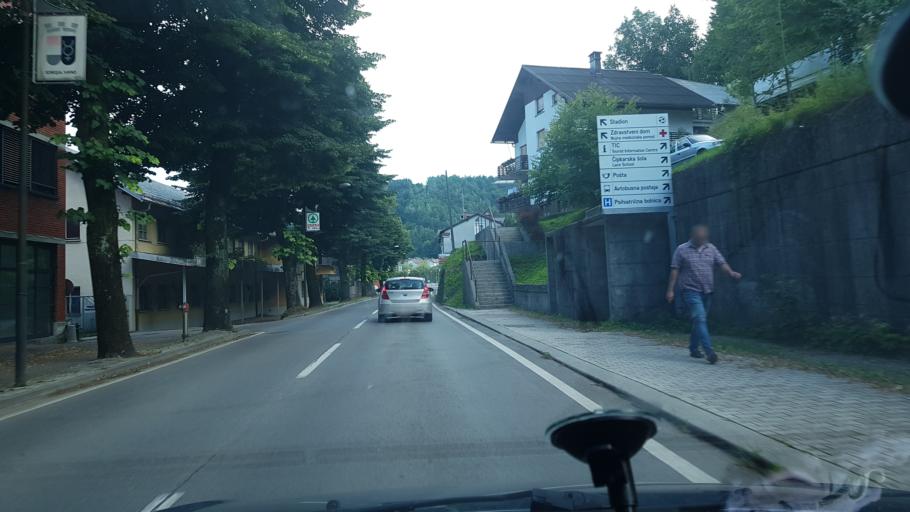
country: SI
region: Idrija
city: Idrija
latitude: 46.0053
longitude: 14.0280
